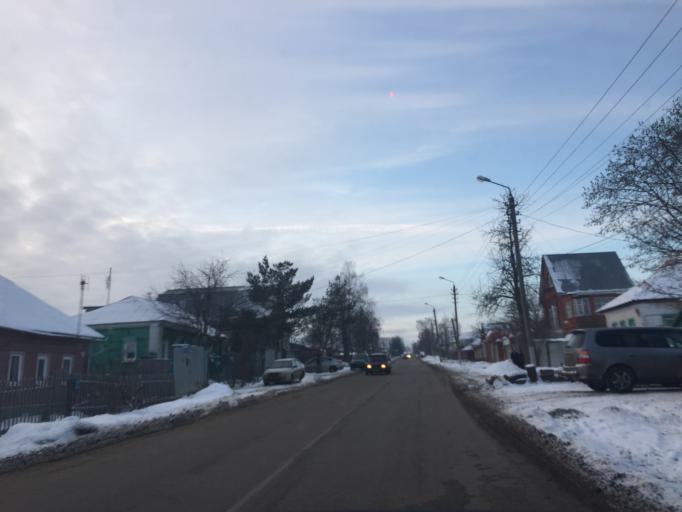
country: RU
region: Tula
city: Gorelki
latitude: 54.2332
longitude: 37.6400
